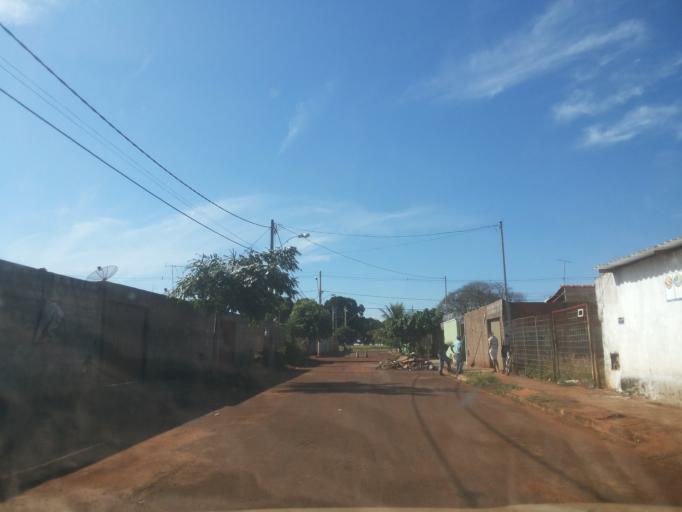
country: BR
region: Minas Gerais
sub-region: Centralina
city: Centralina
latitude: -18.7164
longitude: -49.2048
